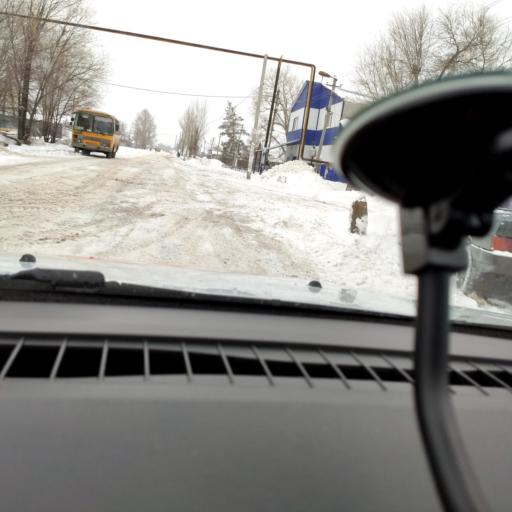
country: RU
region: Samara
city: Dubovyy Umet
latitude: 53.0387
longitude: 50.2428
